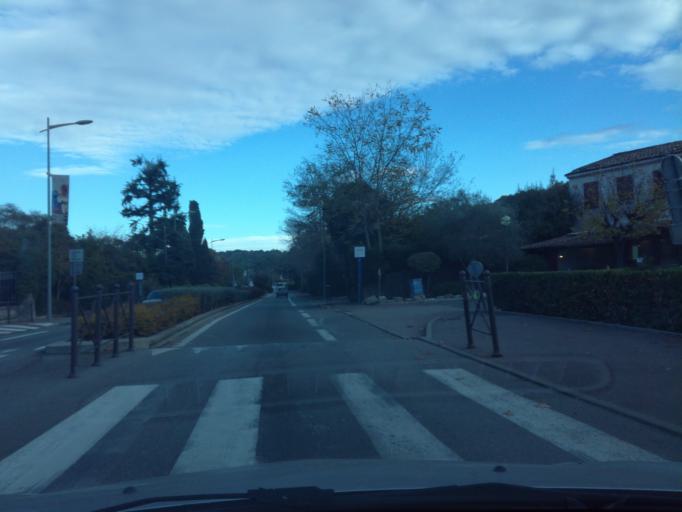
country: FR
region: Provence-Alpes-Cote d'Azur
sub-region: Departement des Alpes-Maritimes
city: Mougins
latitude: 43.6022
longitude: 7.0162
